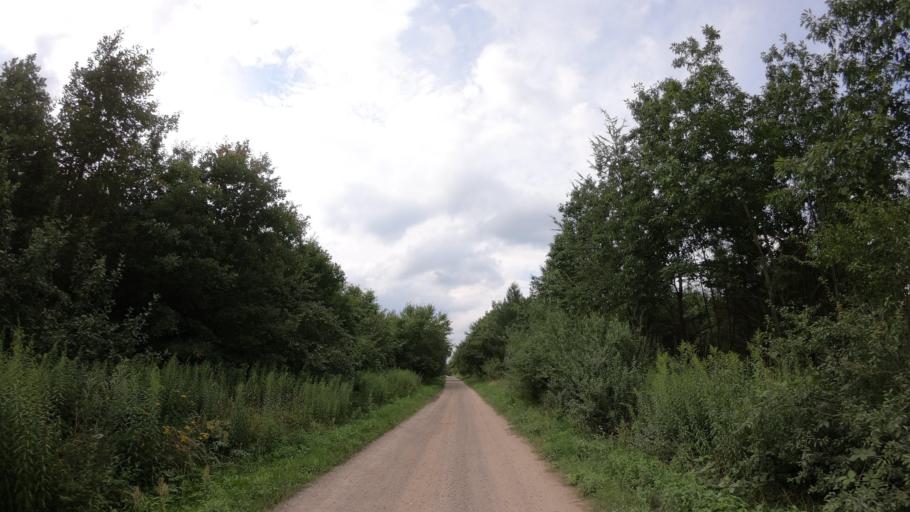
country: PL
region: West Pomeranian Voivodeship
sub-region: Powiat drawski
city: Kalisz Pomorski
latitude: 53.2866
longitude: 15.9361
